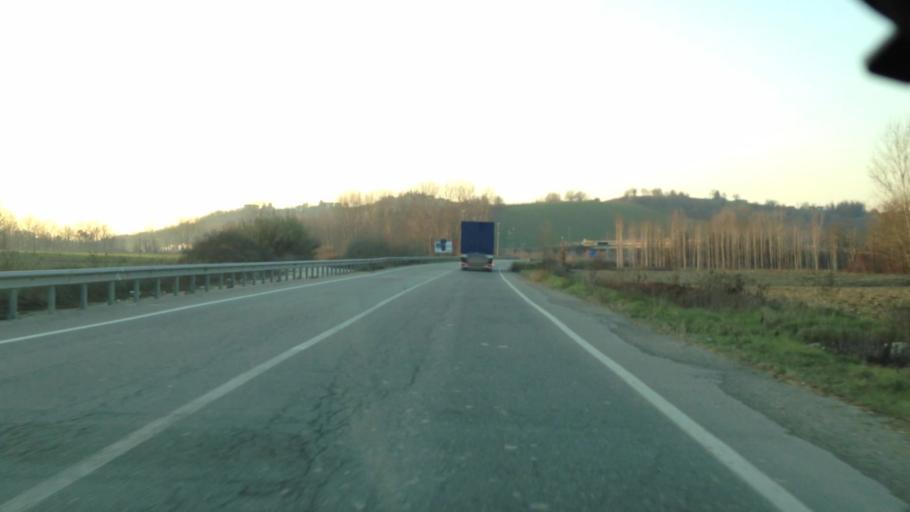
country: IT
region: Piedmont
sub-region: Provincia di Asti
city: Vigliano d'Asti
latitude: 44.8272
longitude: 8.2089
